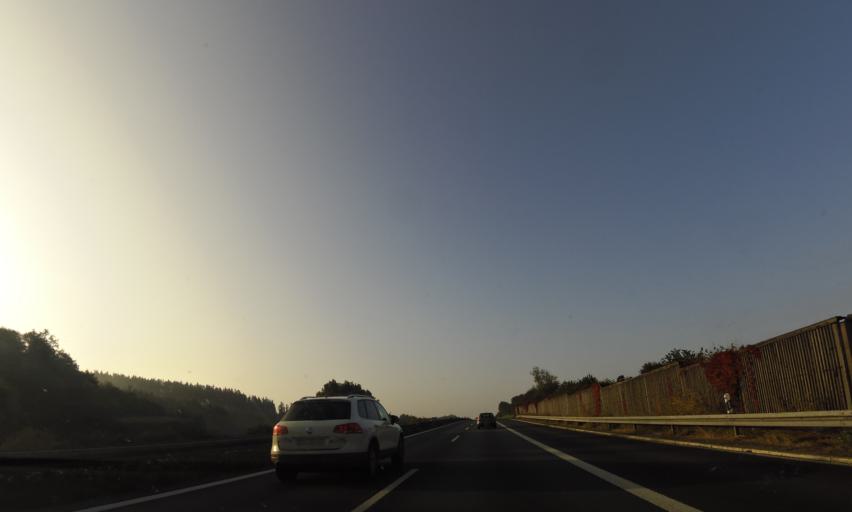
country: DE
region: Saxony
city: Neuensalz
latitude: 50.4836
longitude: 12.1864
